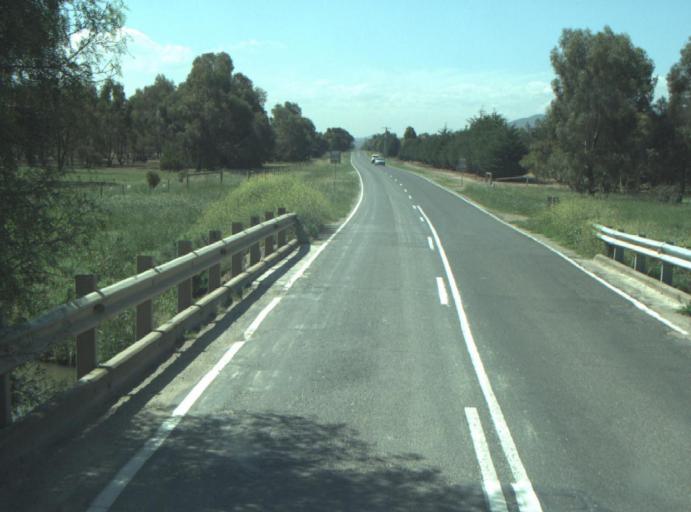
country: AU
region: Victoria
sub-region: Greater Geelong
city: Lara
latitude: -38.0168
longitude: 144.3974
